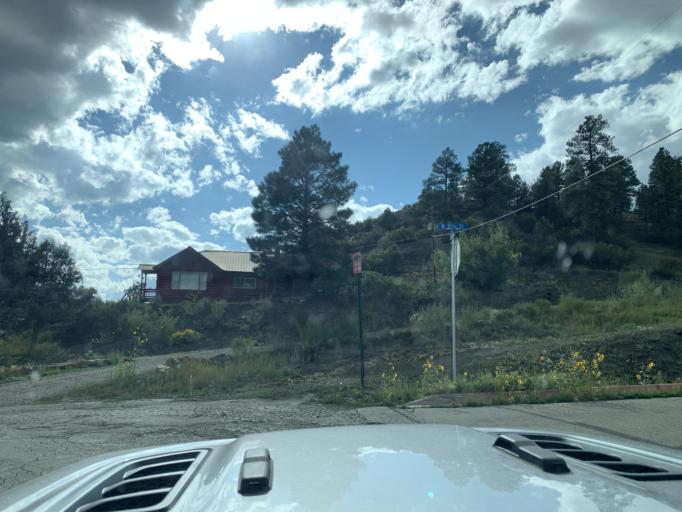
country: US
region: Colorado
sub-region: Archuleta County
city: Pagosa Springs
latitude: 37.2679
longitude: -107.0171
